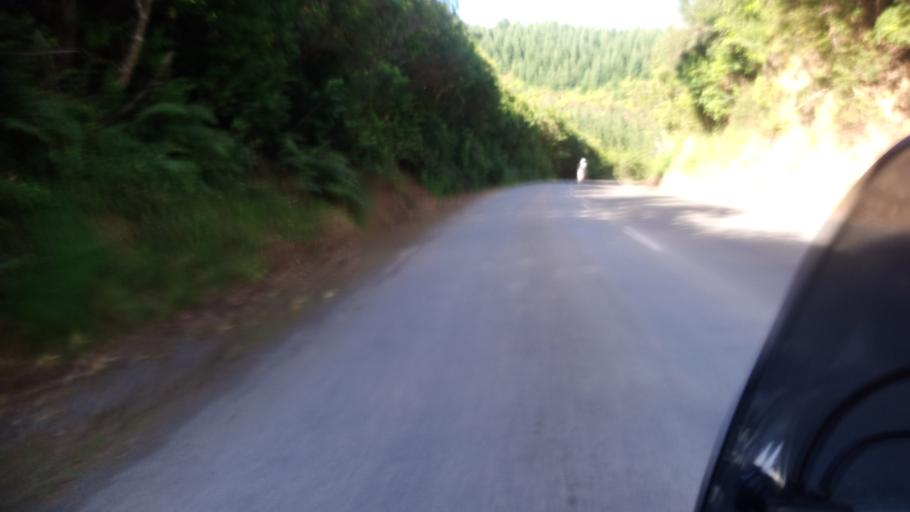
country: NZ
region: Hawke's Bay
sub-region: Wairoa District
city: Wairoa
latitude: -39.0065
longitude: 177.0957
